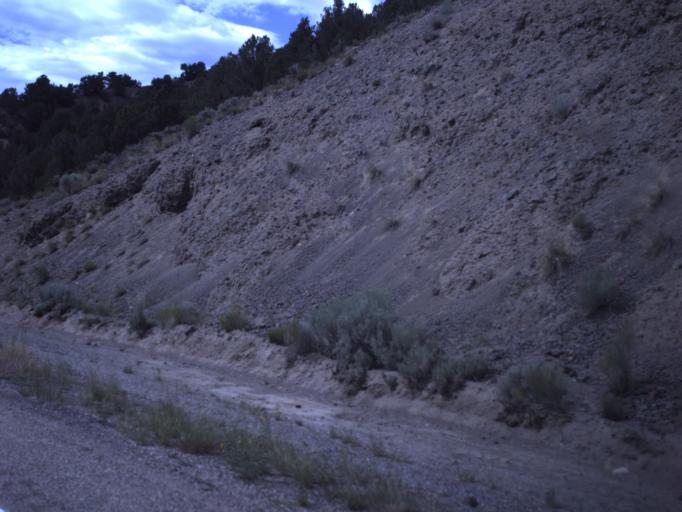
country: US
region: Utah
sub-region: Garfield County
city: Panguitch
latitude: 37.9844
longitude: -112.4883
